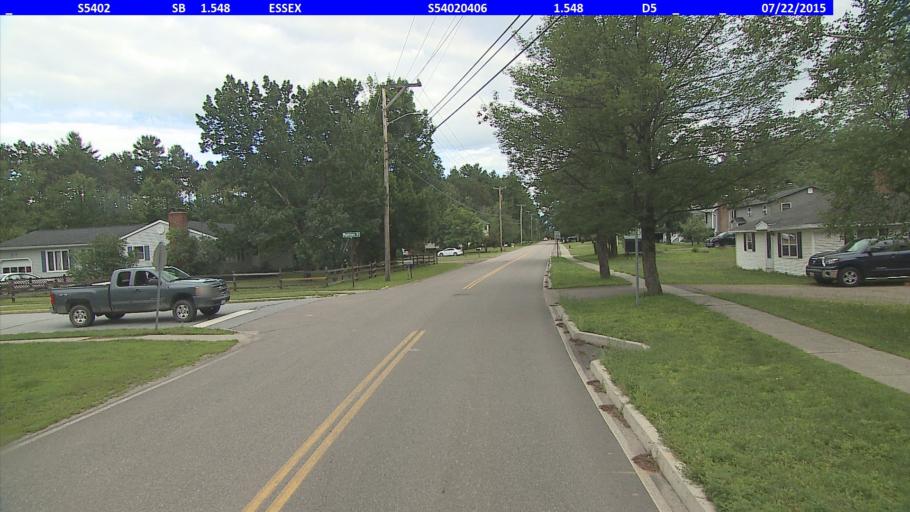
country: US
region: Vermont
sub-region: Chittenden County
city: Jericho
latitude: 44.5005
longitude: -73.0492
